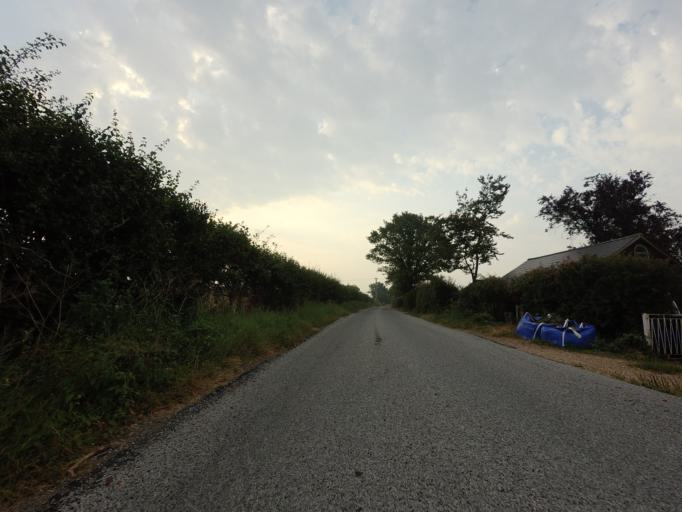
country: GB
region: England
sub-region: Kent
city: Lenham
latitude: 51.1610
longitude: 0.7559
